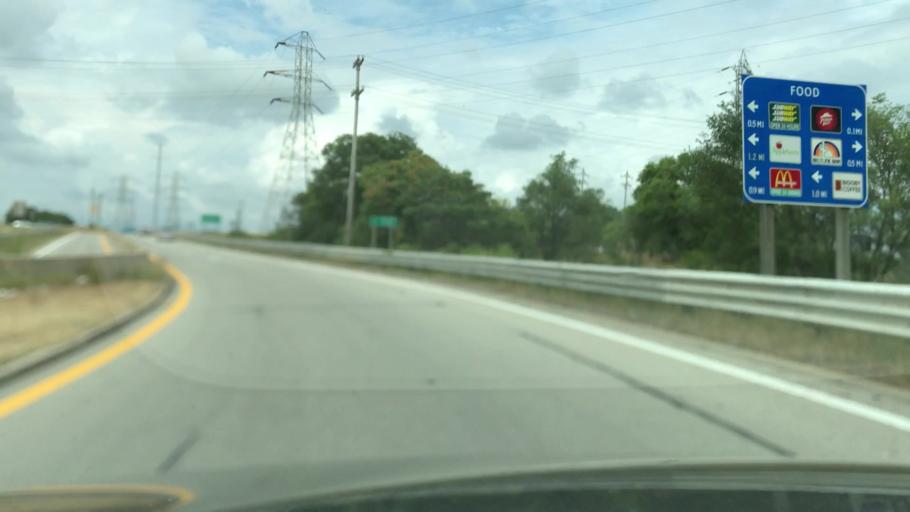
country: US
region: Michigan
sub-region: Kent County
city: Wyoming
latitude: 42.9113
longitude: -85.6761
